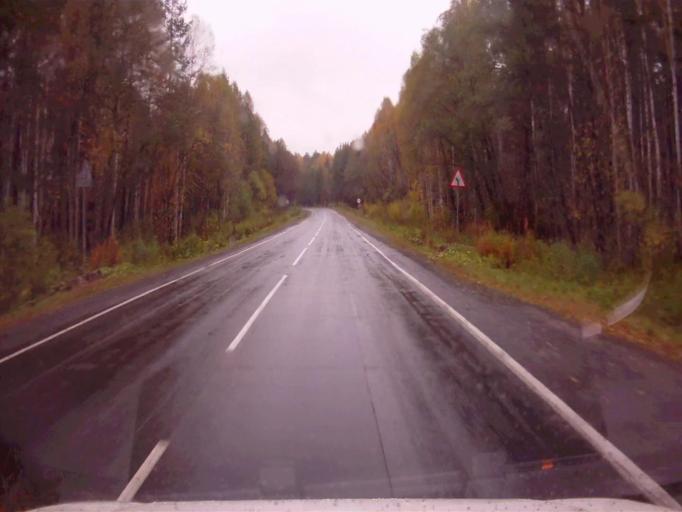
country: RU
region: Chelyabinsk
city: Verkhniy Ufaley
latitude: 55.9558
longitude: 60.3911
